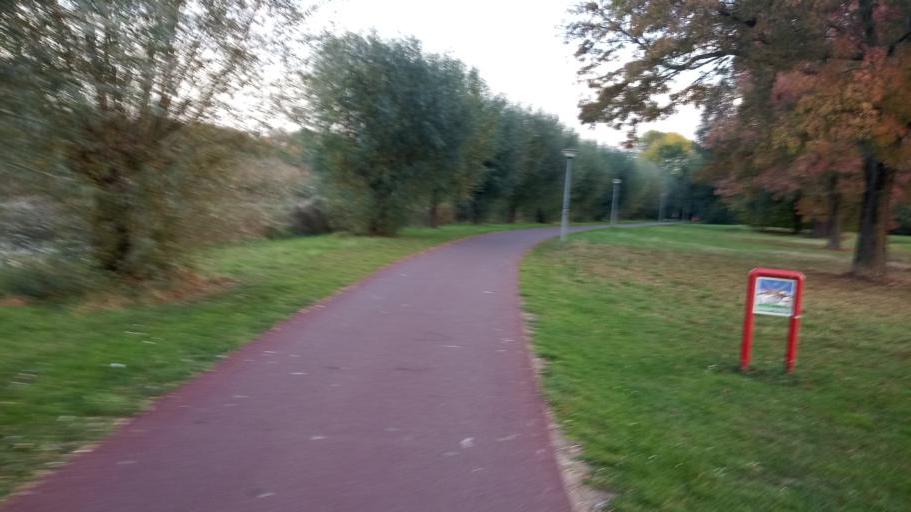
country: NL
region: Gelderland
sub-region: Gemeente Zutphen
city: Zutphen
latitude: 52.1290
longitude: 6.2021
